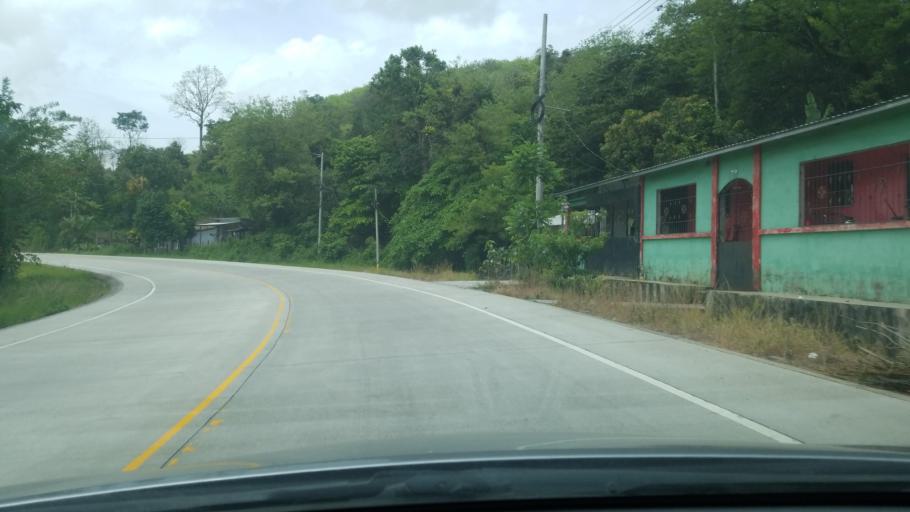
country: HN
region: Copan
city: San Juan de Planes
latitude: 14.9398
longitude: -88.7658
